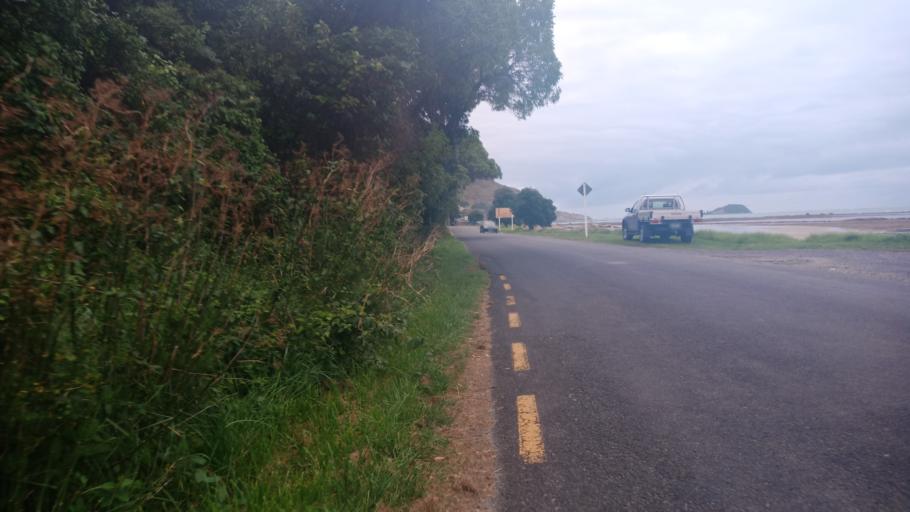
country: NZ
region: Gisborne
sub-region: Gisborne District
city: Gisborne
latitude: -38.6805
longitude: 178.0279
